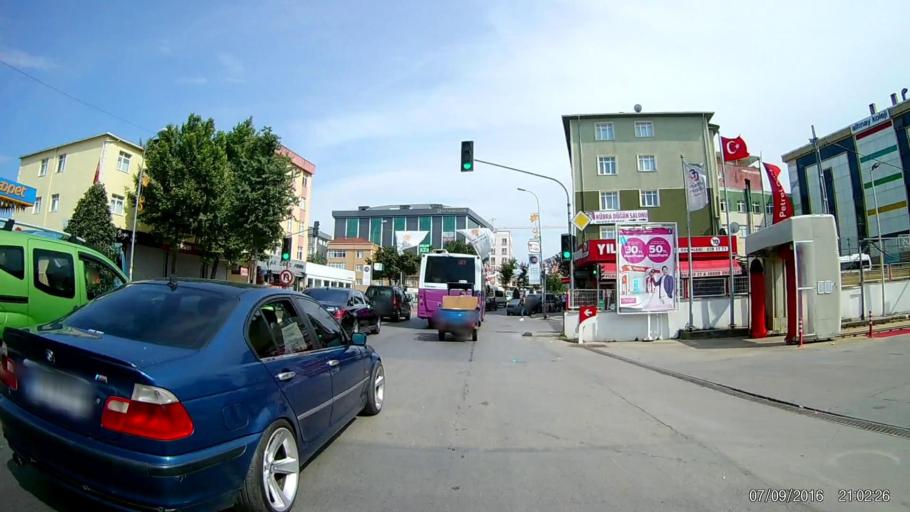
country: TR
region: Istanbul
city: Sultanbeyli
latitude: 40.9716
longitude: 29.2489
